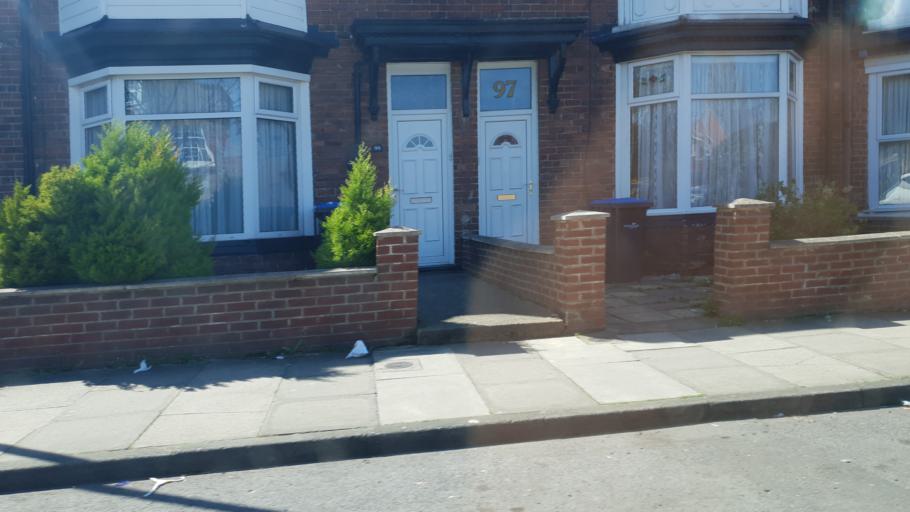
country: GB
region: England
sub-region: Middlesbrough
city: Middlesbrough
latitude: 54.5558
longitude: -1.2465
